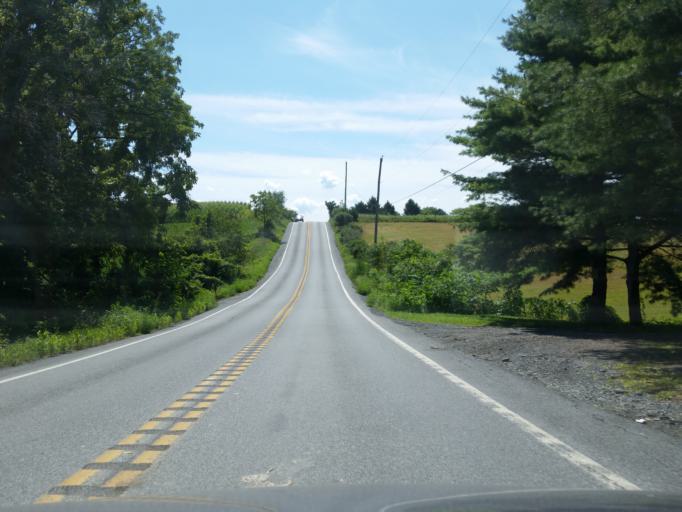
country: US
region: Pennsylvania
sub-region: Lebanon County
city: Palmyra
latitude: 40.3662
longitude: -76.6279
